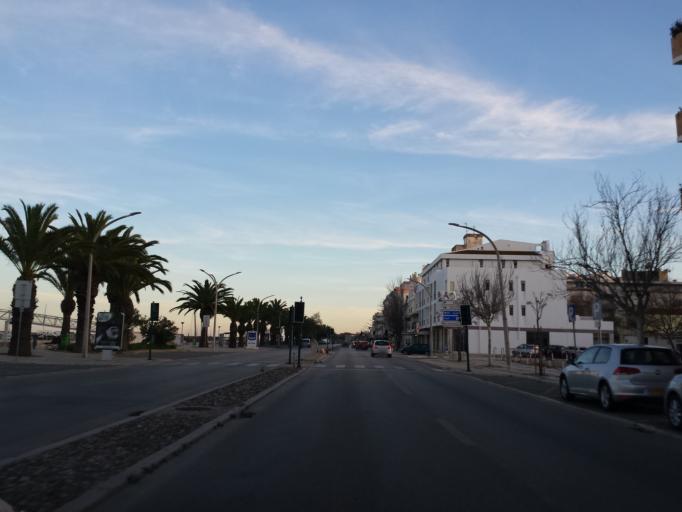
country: PT
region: Faro
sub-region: Lagos
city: Lagos
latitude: 37.1081
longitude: -8.6756
